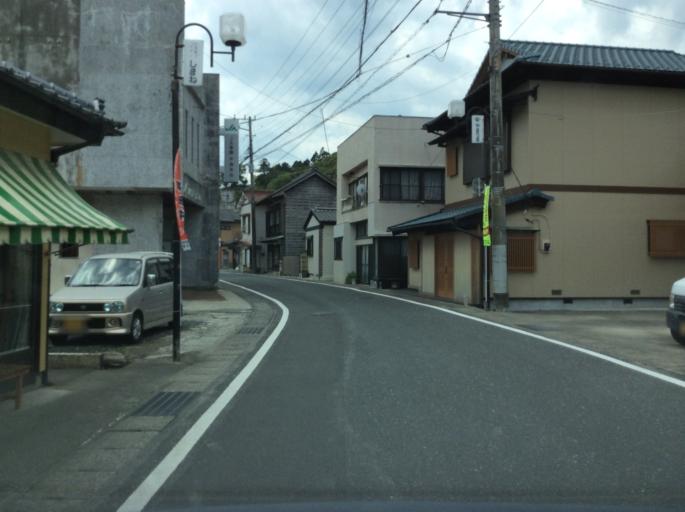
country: JP
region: Ibaraki
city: Kitaibaraki
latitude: 36.8558
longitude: 140.7921
